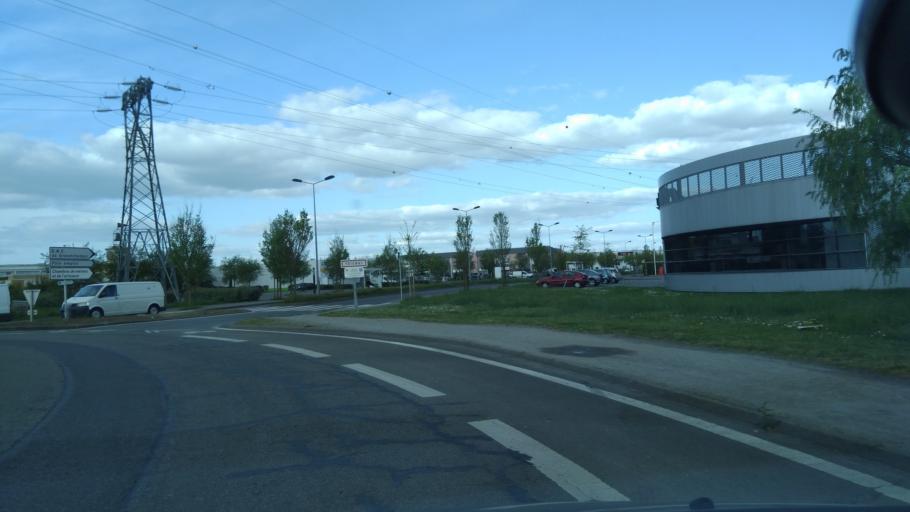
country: FR
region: Pays de la Loire
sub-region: Departement de la Loire-Atlantique
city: Saint-Nazaire
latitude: 47.2933
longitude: -2.2082
